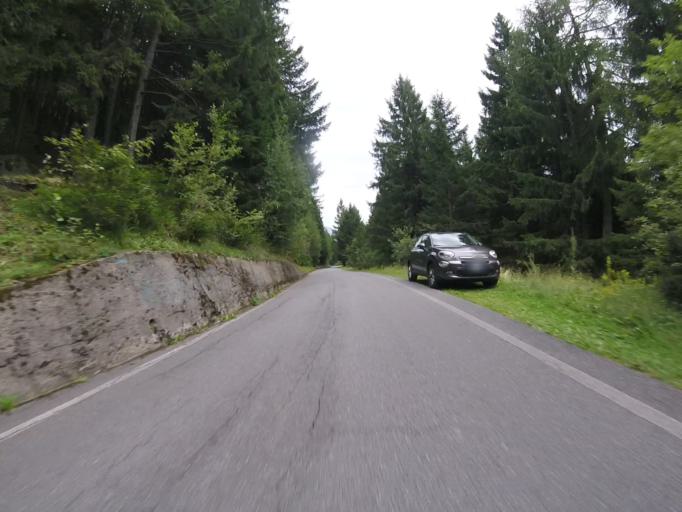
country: IT
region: Lombardy
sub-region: Provincia di Brescia
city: Monno
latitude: 46.2224
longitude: 10.3278
